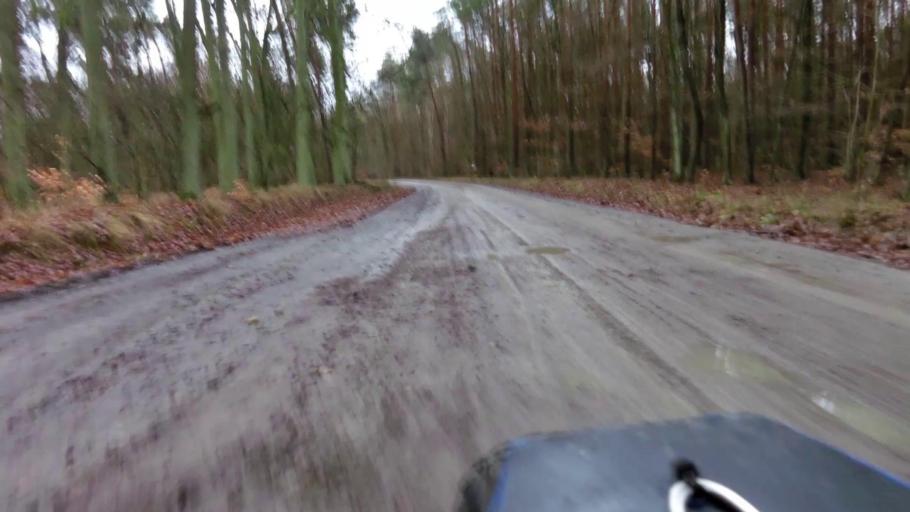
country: PL
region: Lubusz
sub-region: Powiat gorzowski
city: Witnica
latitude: 52.6944
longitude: 14.8480
